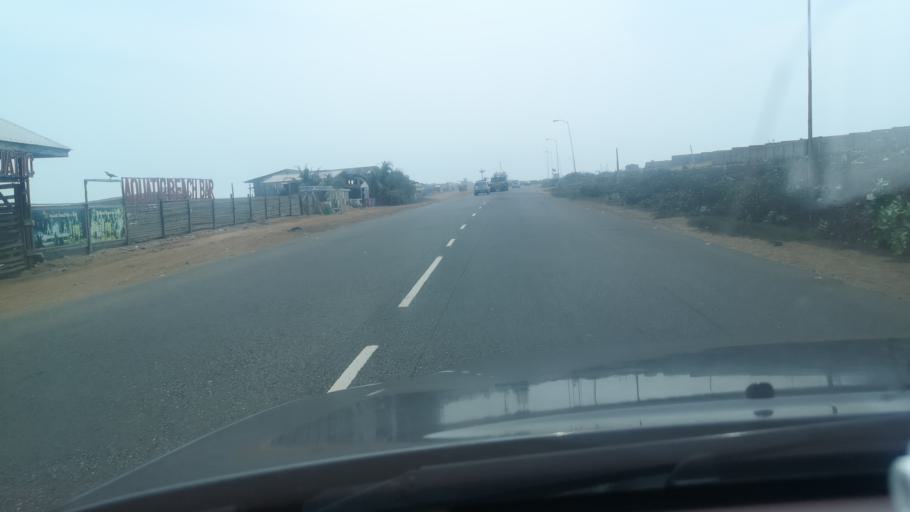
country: GH
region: Greater Accra
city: Nungua
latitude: 5.6108
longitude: -0.0481
